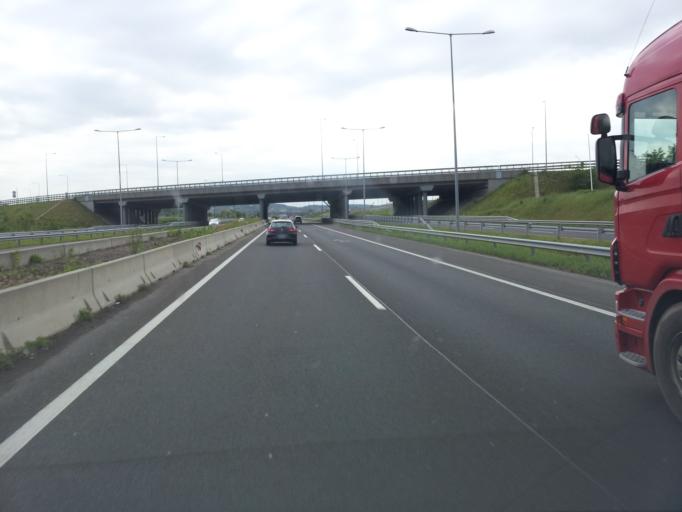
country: HU
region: Pest
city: Szada
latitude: 47.6130
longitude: 19.3150
